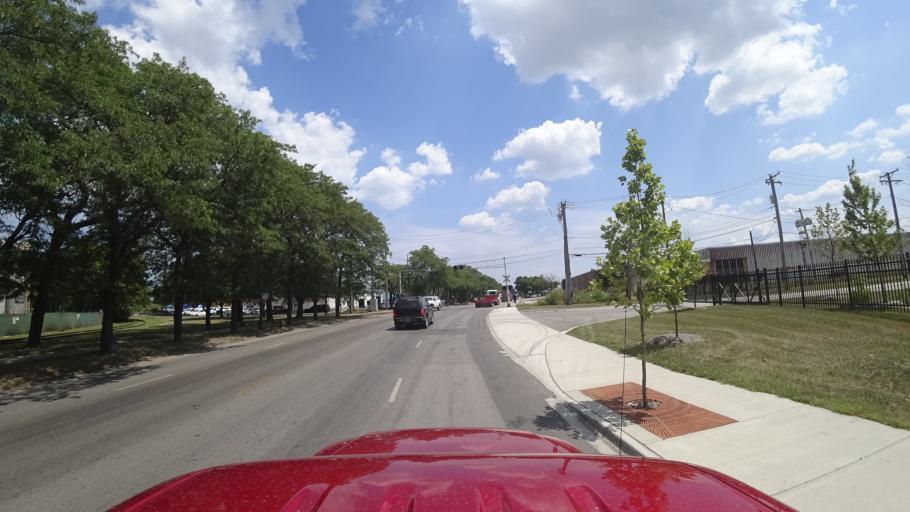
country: US
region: Illinois
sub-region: Cook County
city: Chicago
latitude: 41.8158
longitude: -87.6610
